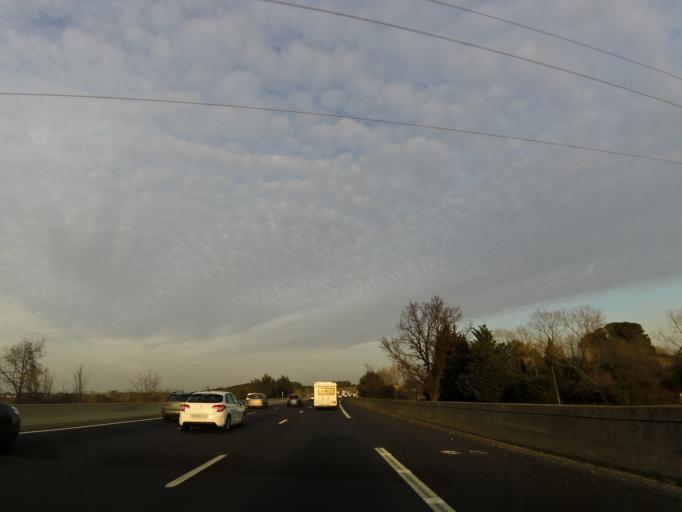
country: FR
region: Languedoc-Roussillon
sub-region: Departement de l'Herault
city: Lunel-Viel
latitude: 43.6959
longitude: 4.0888
